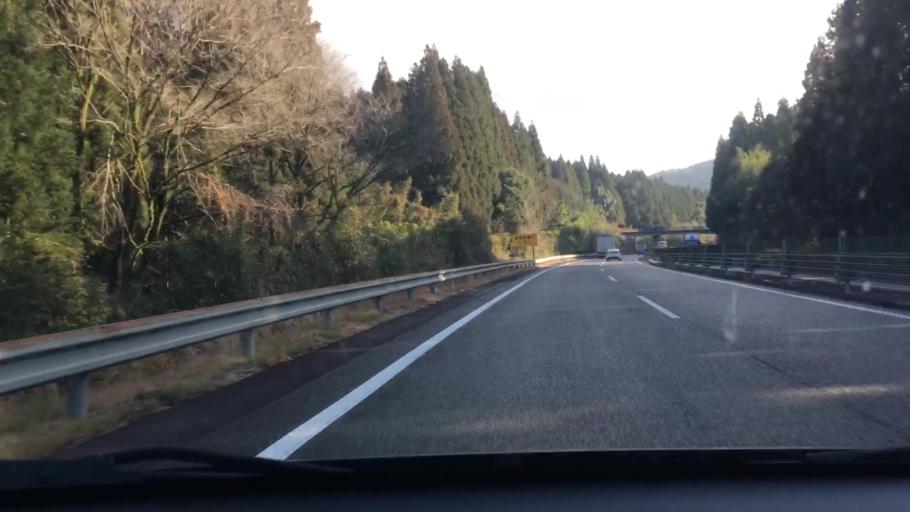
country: JP
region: Kagoshima
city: Okuchi-shinohara
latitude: 32.0003
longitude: 130.7581
